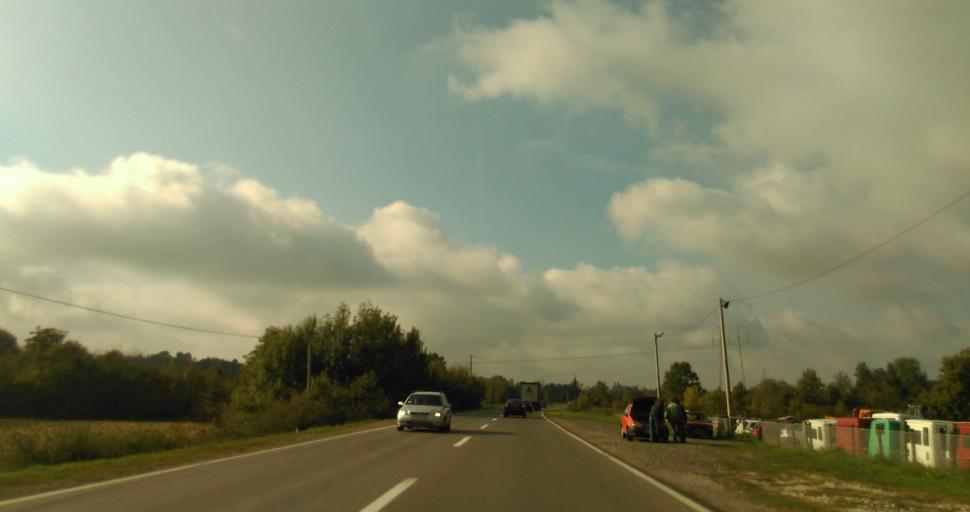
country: RS
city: Stepojevac
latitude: 44.5002
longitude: 20.2895
